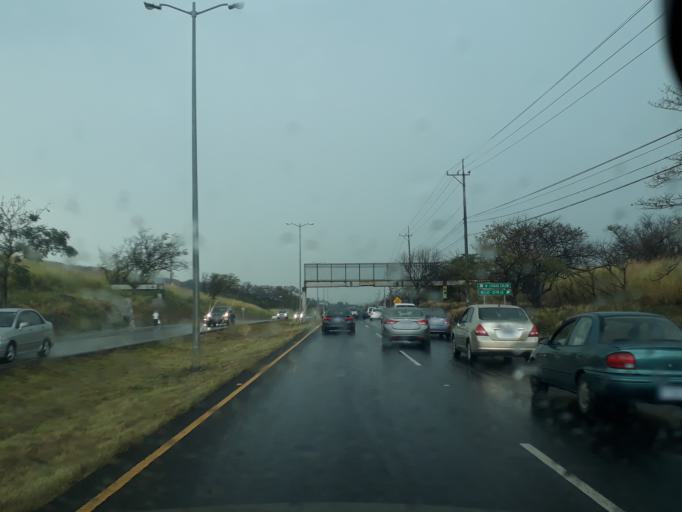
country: CR
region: San Jose
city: Santa Ana
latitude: 9.9424
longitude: -84.1963
